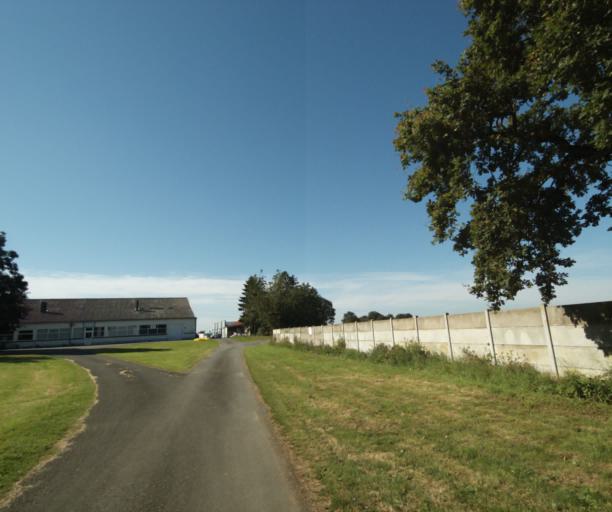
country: FR
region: Pays de la Loire
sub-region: Departement de la Mayenne
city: Laval
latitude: 48.0366
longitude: -0.7411
